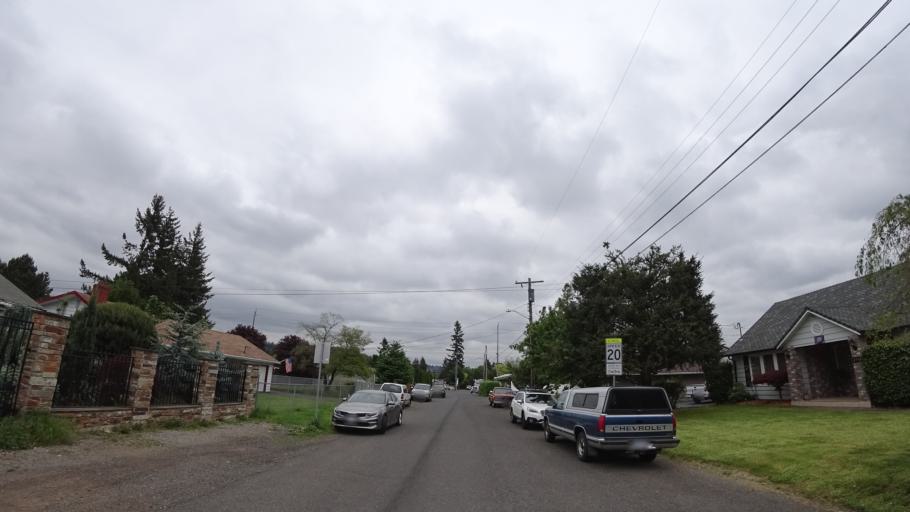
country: US
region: Oregon
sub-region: Multnomah County
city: Lents
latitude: 45.5052
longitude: -122.5228
